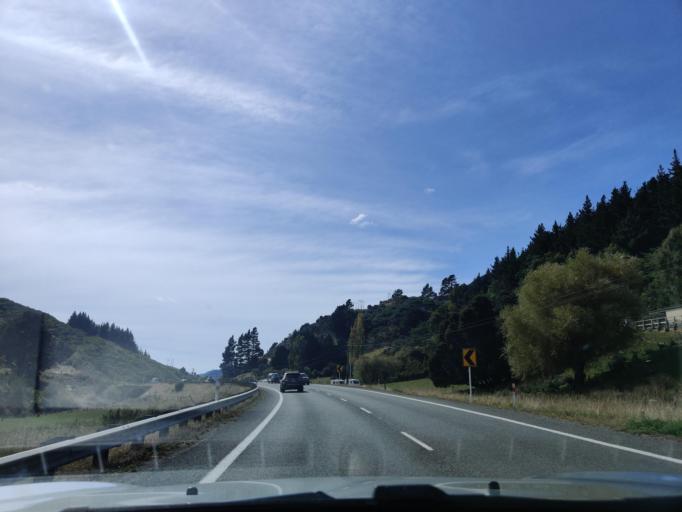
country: NZ
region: Marlborough
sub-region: Marlborough District
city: Picton
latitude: -41.3087
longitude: 173.9837
